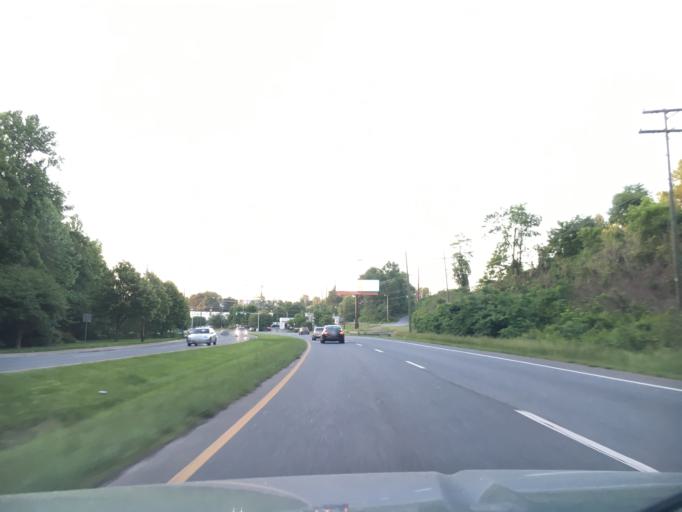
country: US
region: Virginia
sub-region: City of Lynchburg
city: West Lynchburg
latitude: 37.3570
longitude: -79.1811
